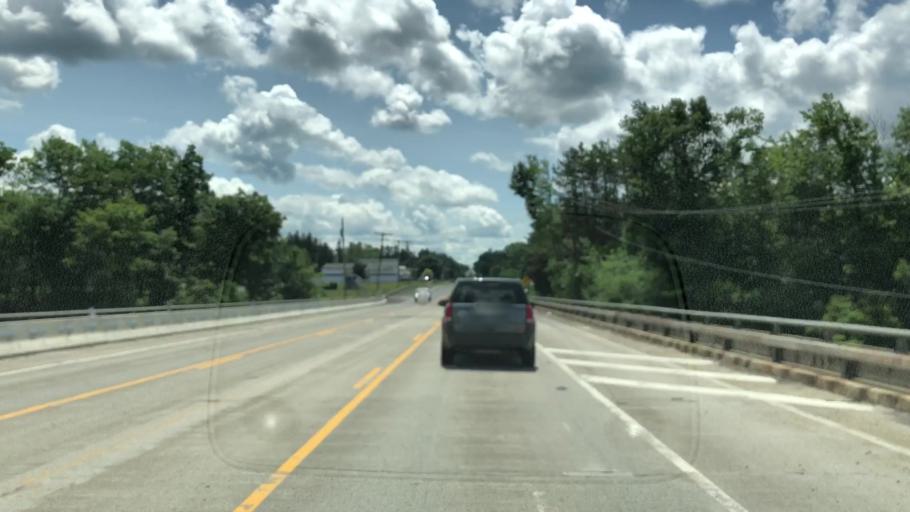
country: US
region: New York
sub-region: Erie County
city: Elma Center
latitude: 42.8159
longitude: -78.6969
